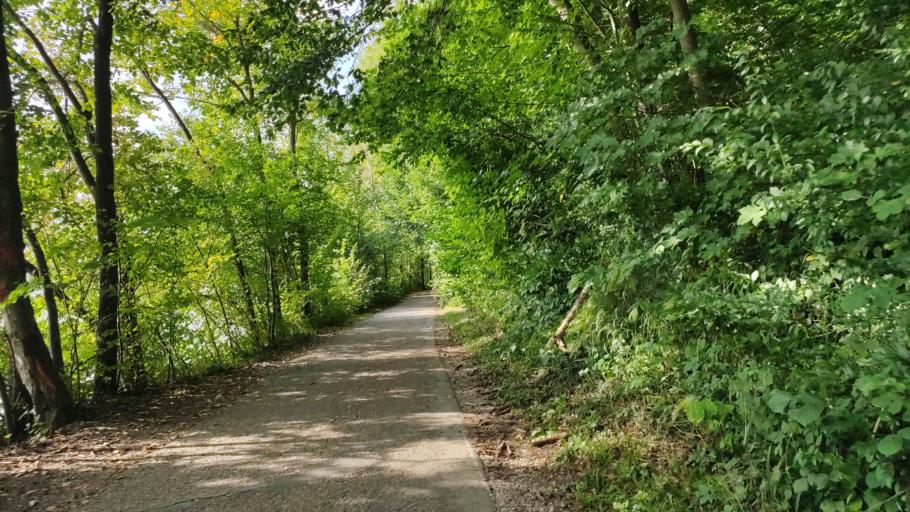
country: DE
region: Bavaria
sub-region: Upper Bavaria
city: Kaufering
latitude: 48.1131
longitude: 10.8662
